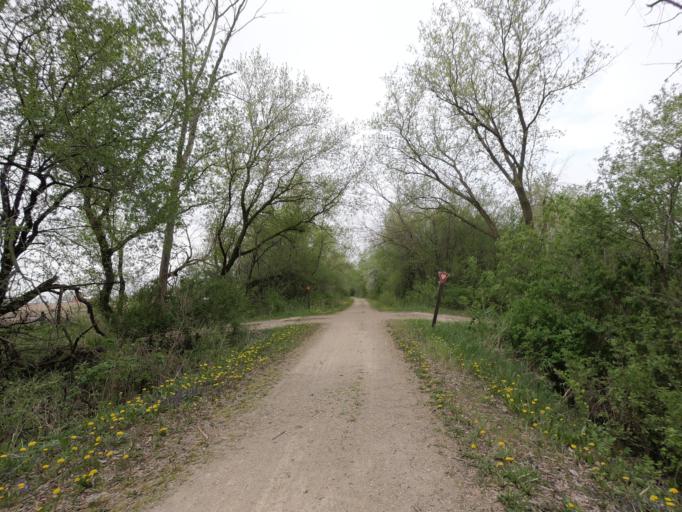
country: US
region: Wisconsin
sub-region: Jefferson County
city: Johnson Creek
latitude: 43.0372
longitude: -88.7671
